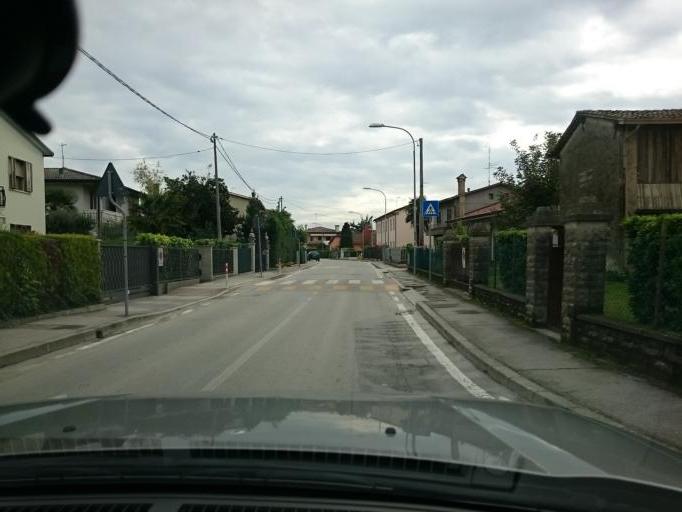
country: IT
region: Veneto
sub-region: Provincia di Padova
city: Arzergrande
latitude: 45.2855
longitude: 12.0572
